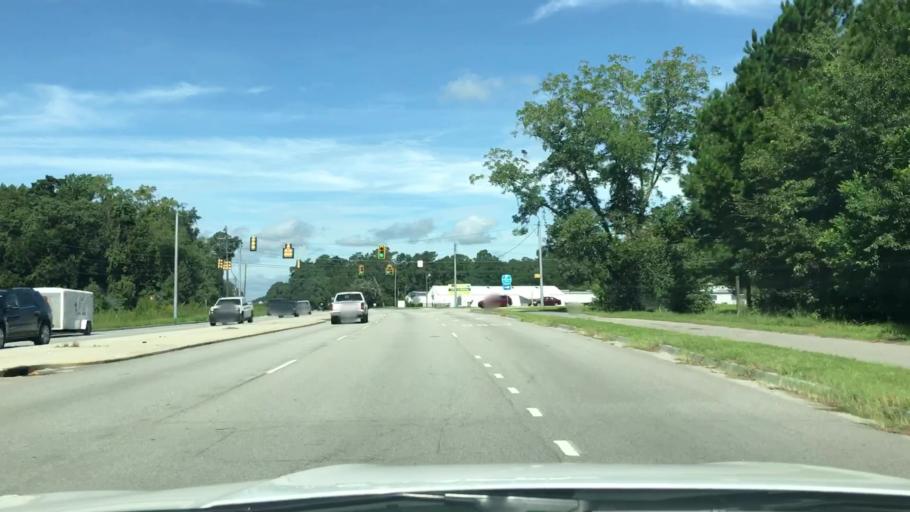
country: US
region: South Carolina
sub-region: Dorchester County
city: Centerville
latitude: 32.9702
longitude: -80.2088
